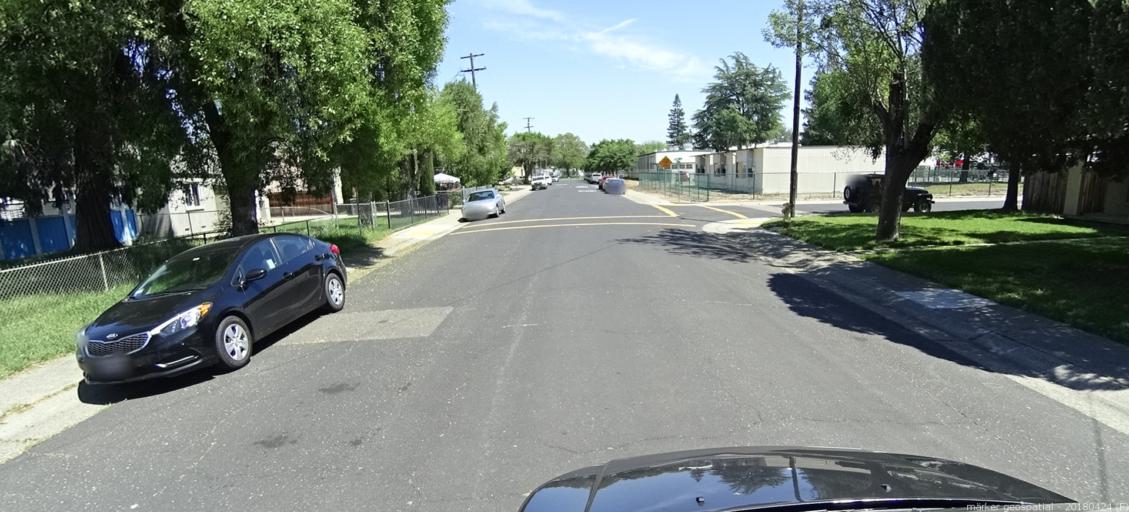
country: US
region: California
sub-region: Yolo County
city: West Sacramento
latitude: 38.5784
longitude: -121.5328
